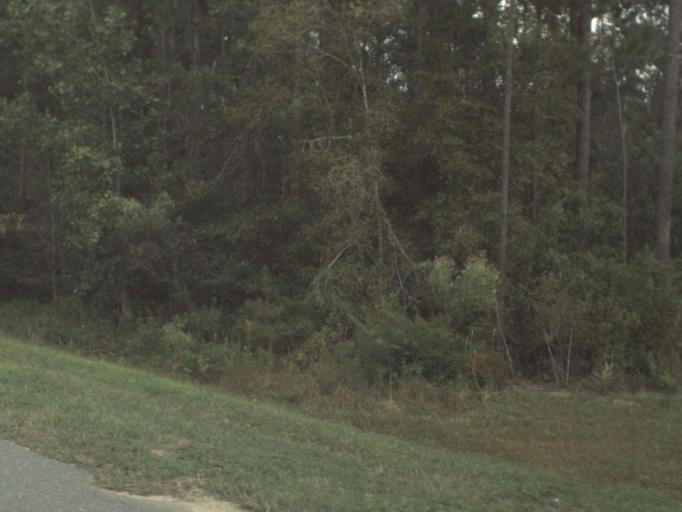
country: US
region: Florida
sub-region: Calhoun County
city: Blountstown
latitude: 30.4309
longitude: -85.1902
